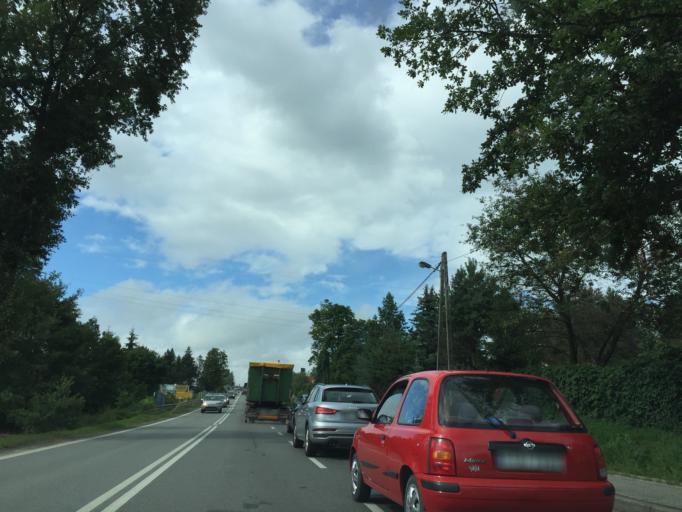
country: PL
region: Lesser Poland Voivodeship
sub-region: Powiat nowotarski
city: Rokiciny
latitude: 49.6043
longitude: 19.9288
